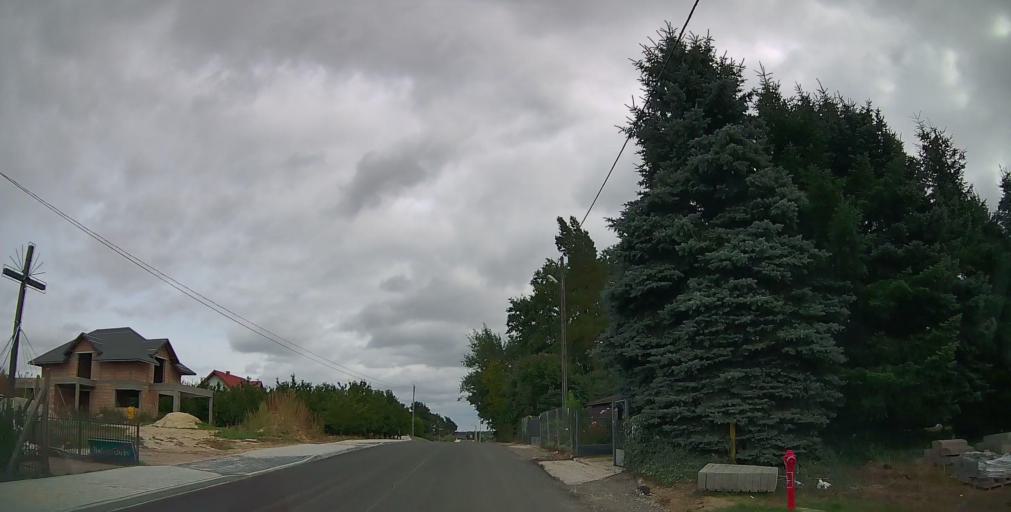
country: PL
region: Masovian Voivodeship
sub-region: Powiat grojecki
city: Belsk Duzy
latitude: 51.8143
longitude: 20.8305
